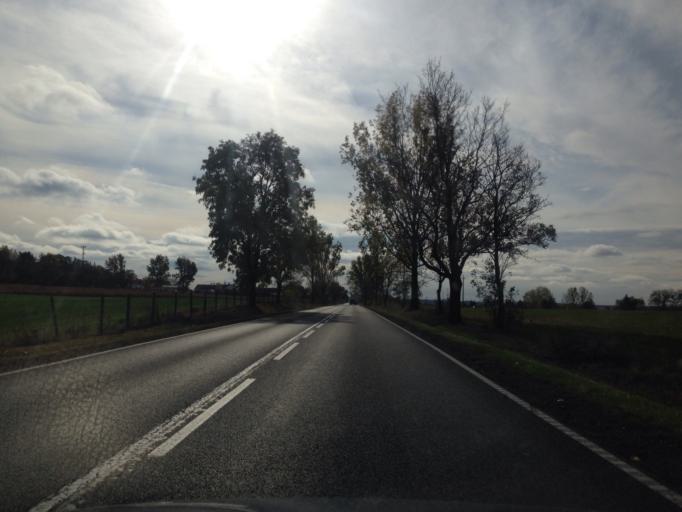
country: PL
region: Kujawsko-Pomorskie
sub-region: Powiat brodnicki
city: Brzozie
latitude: 53.3033
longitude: 19.5058
